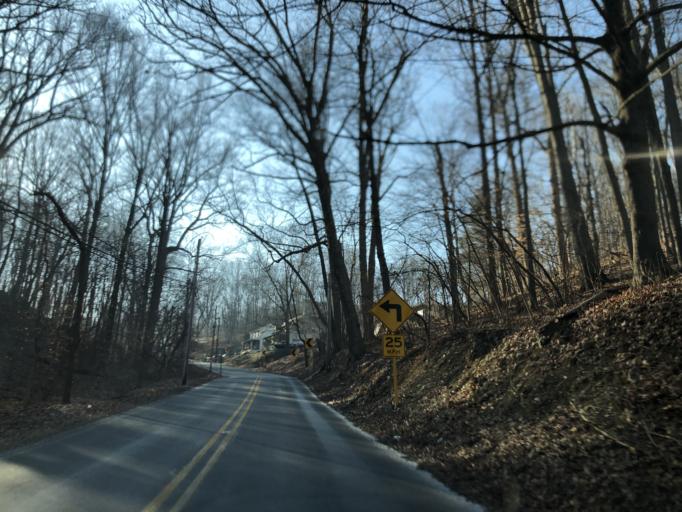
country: US
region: Pennsylvania
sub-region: Chester County
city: Downingtown
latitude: 39.9930
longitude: -75.7121
